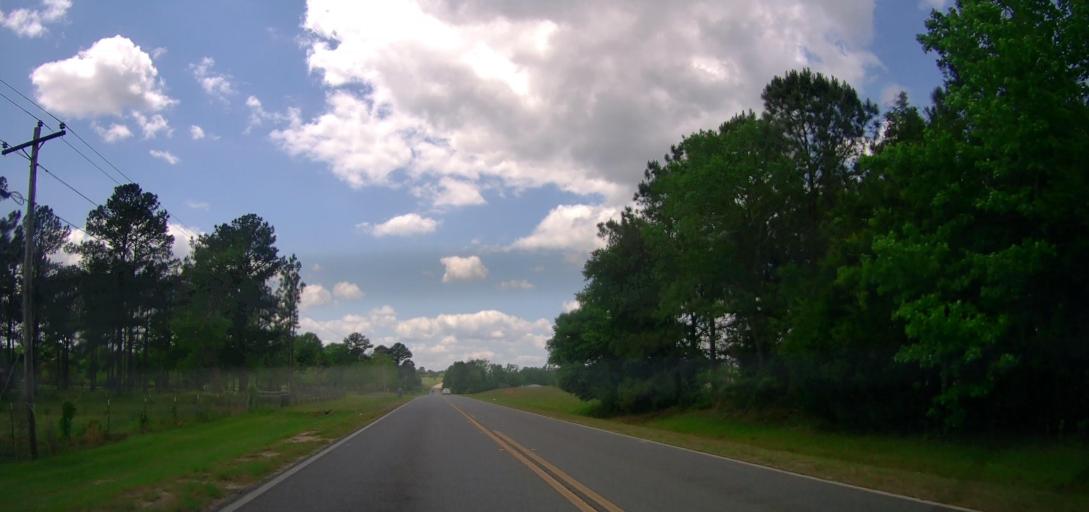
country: US
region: Georgia
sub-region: Laurens County
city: East Dublin
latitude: 32.5185
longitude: -82.7886
